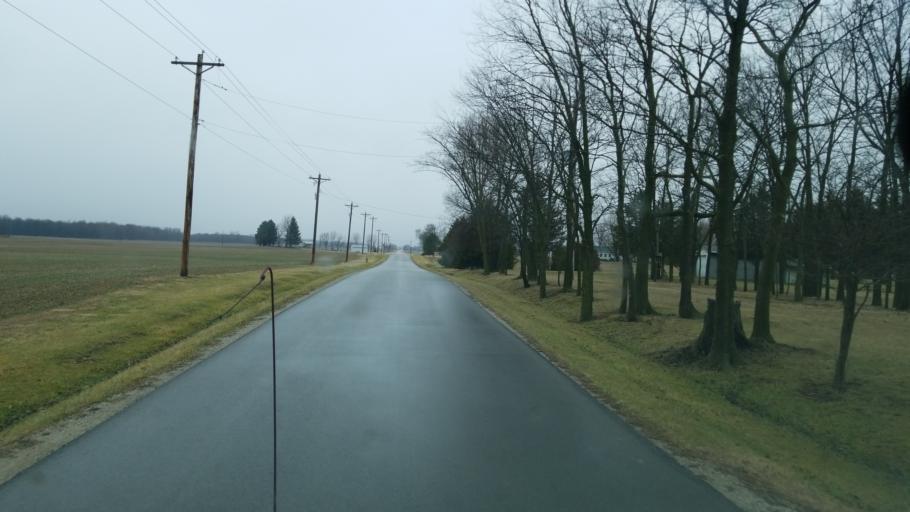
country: US
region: Ohio
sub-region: Crawford County
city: Bucyrus
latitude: 40.8392
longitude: -83.1122
